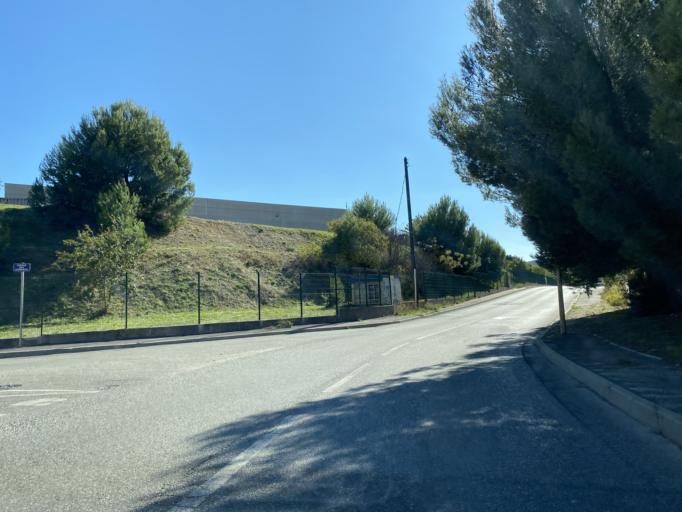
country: FR
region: Provence-Alpes-Cote d'Azur
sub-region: Departement des Bouches-du-Rhone
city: La Ciotat
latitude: 43.2053
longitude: 5.6005
